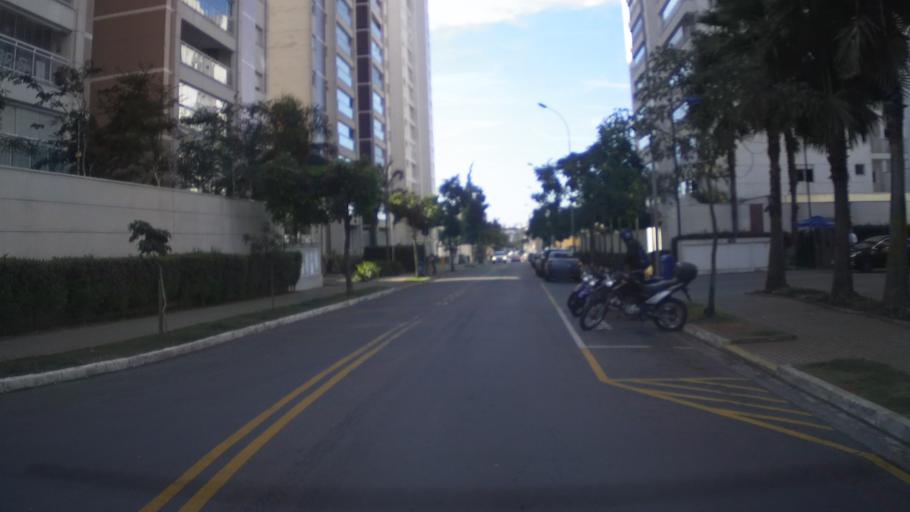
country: BR
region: Sao Paulo
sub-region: Sao Caetano Do Sul
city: Sao Caetano do Sul
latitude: -23.6250
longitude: -46.5787
